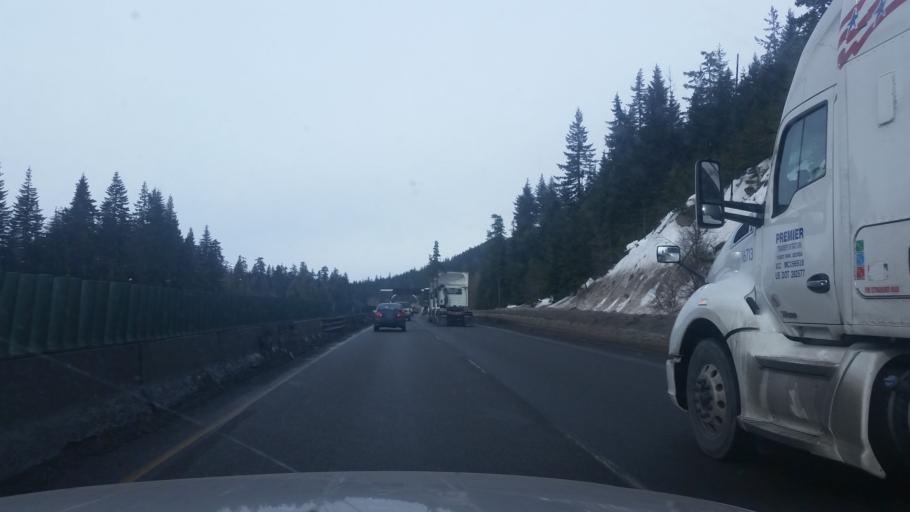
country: US
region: Washington
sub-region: Kittitas County
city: Cle Elum
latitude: 47.3176
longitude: -121.3191
